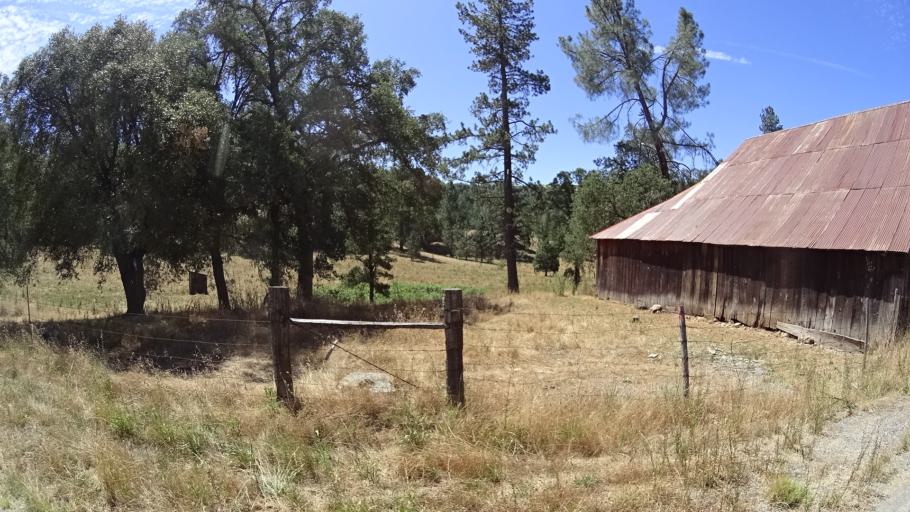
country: US
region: California
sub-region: Calaveras County
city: Mountain Ranch
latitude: 38.3387
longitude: -120.4848
